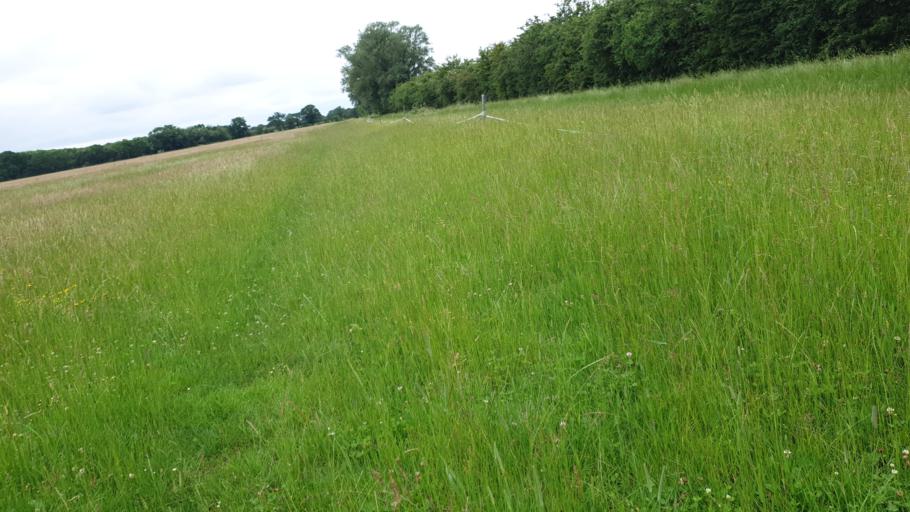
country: GB
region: England
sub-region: Essex
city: Great Bentley
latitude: 51.8879
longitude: 1.0671
